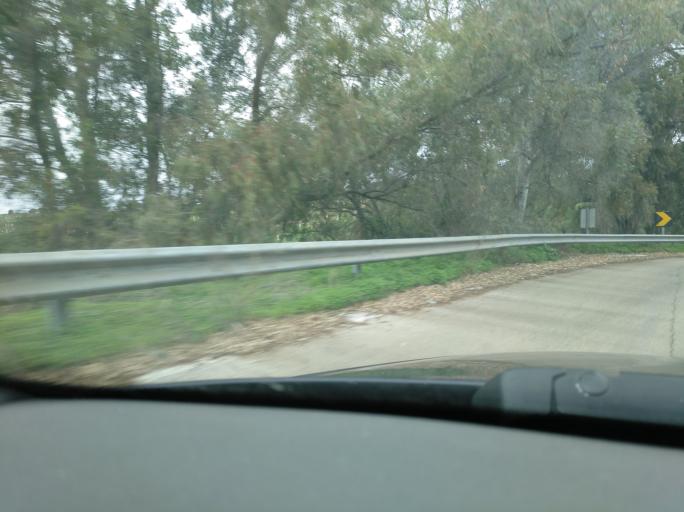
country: PT
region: Faro
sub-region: Vila Real de Santo Antonio
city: Monte Gordo
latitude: 37.2034
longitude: -7.4869
